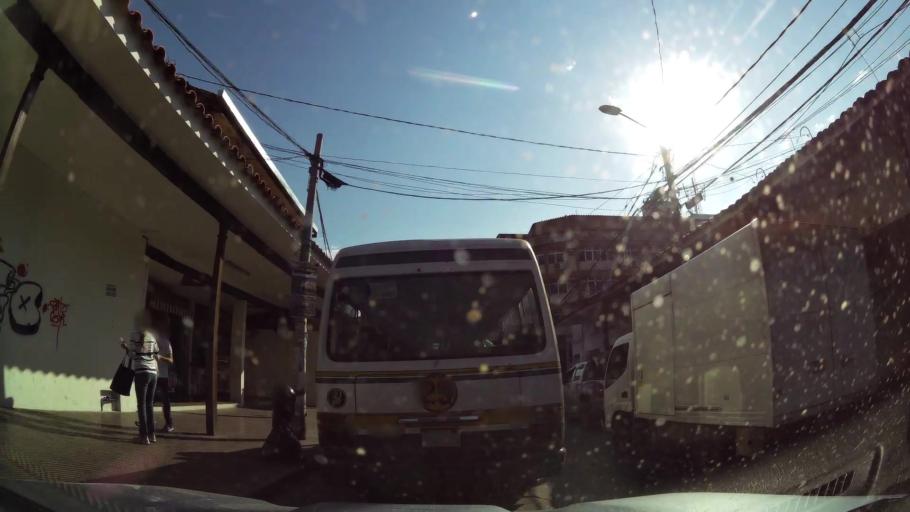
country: BO
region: Santa Cruz
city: Santa Cruz de la Sierra
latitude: -17.7809
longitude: -63.1848
